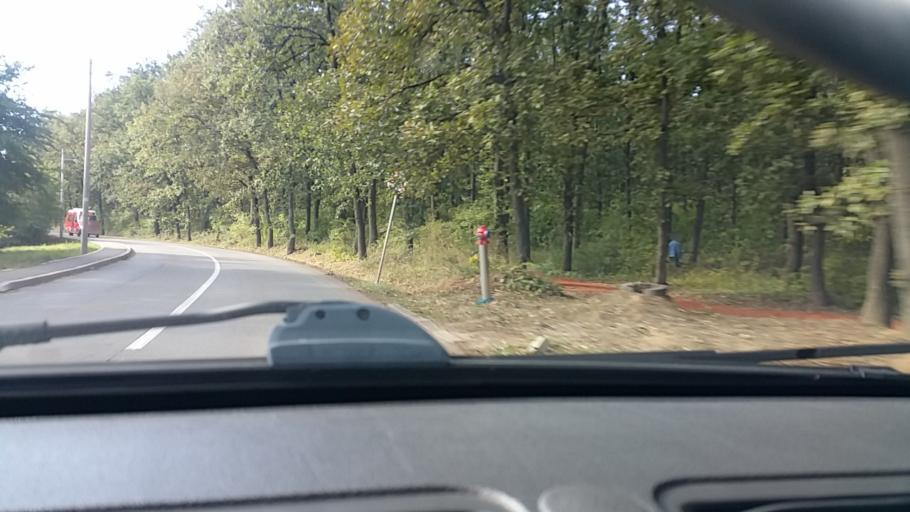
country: RS
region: Central Serbia
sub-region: Belgrade
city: Rakovica
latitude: 44.7437
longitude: 20.4619
